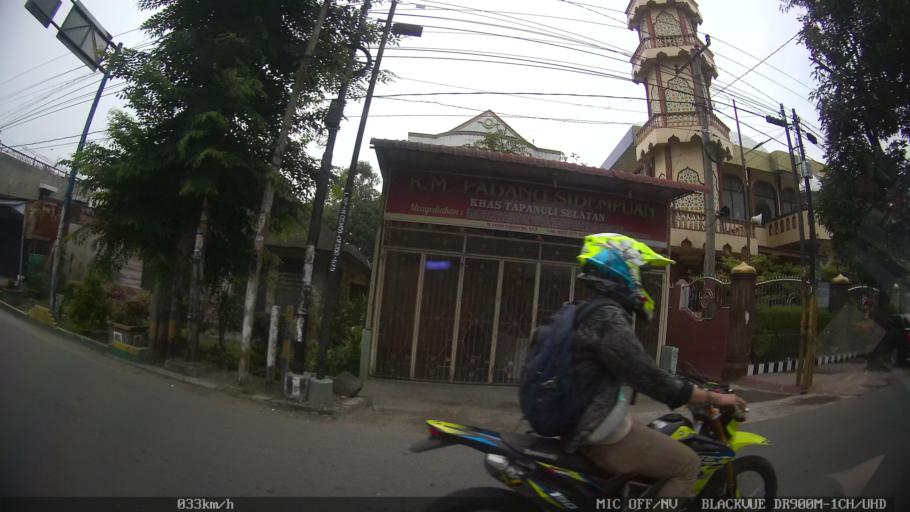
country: ID
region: North Sumatra
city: Medan
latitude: 3.5972
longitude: 98.7159
